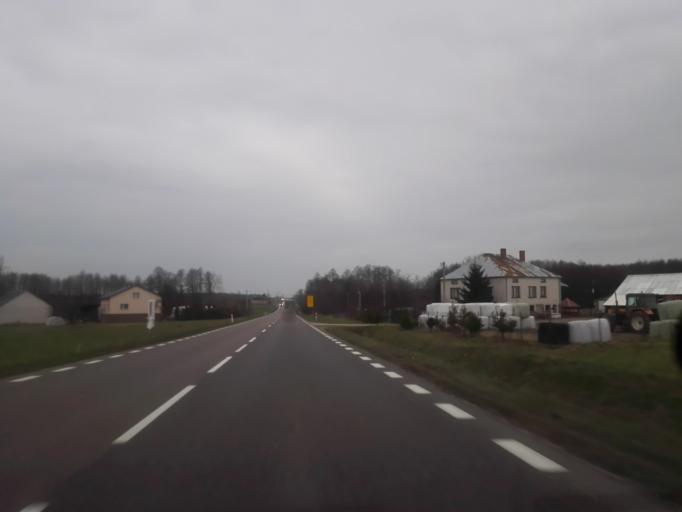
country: PL
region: Podlasie
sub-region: Powiat grajewski
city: Szczuczyn
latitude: 53.4919
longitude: 22.2246
